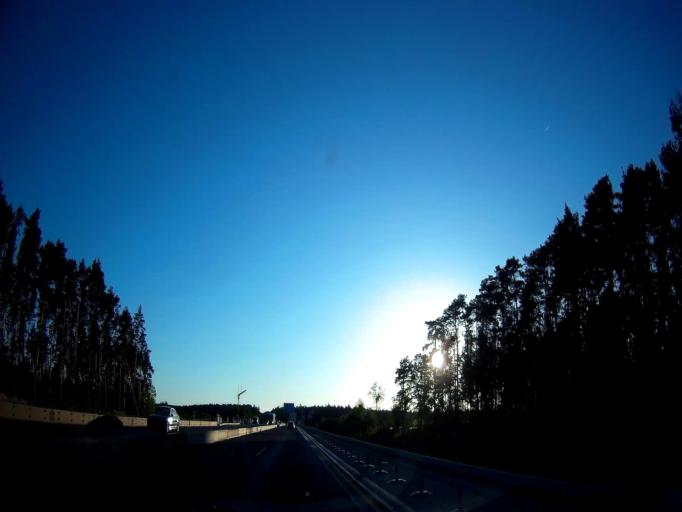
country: DE
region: Bavaria
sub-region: Regierungsbezirk Mittelfranken
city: Schwabach
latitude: 49.3102
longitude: 11.0054
